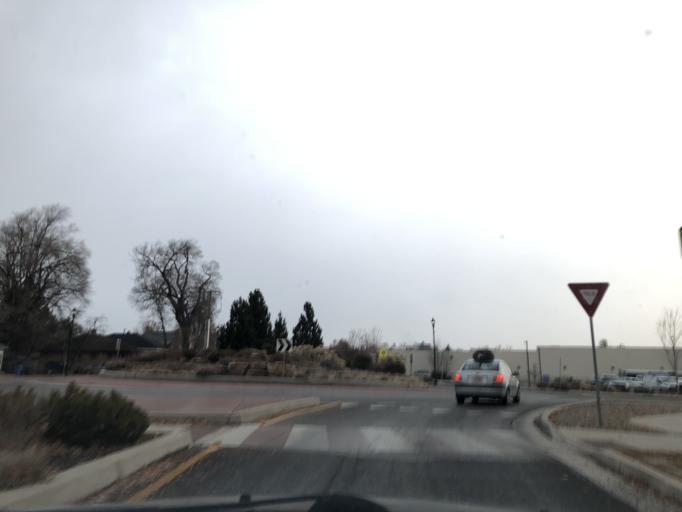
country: US
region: Utah
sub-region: Cache County
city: Logan
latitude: 41.7413
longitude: -111.8296
